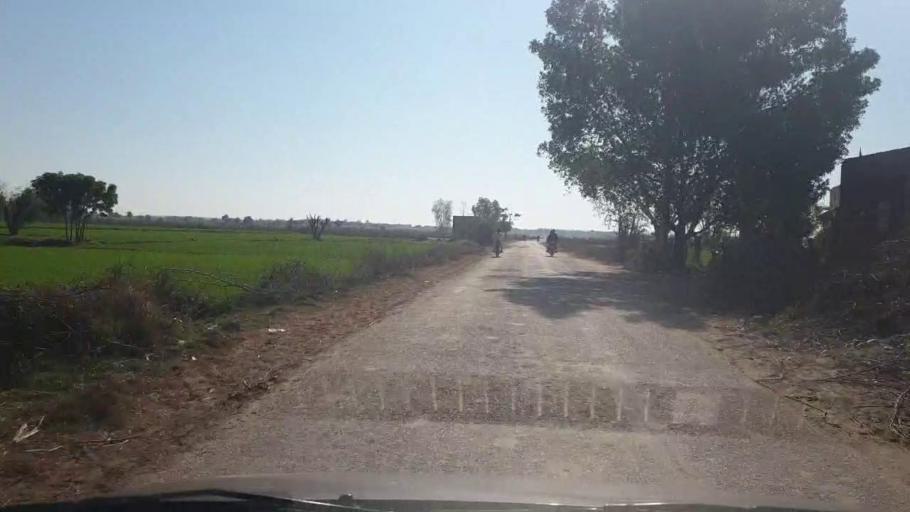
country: PK
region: Sindh
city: Bozdar
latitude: 27.1647
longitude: 68.6442
